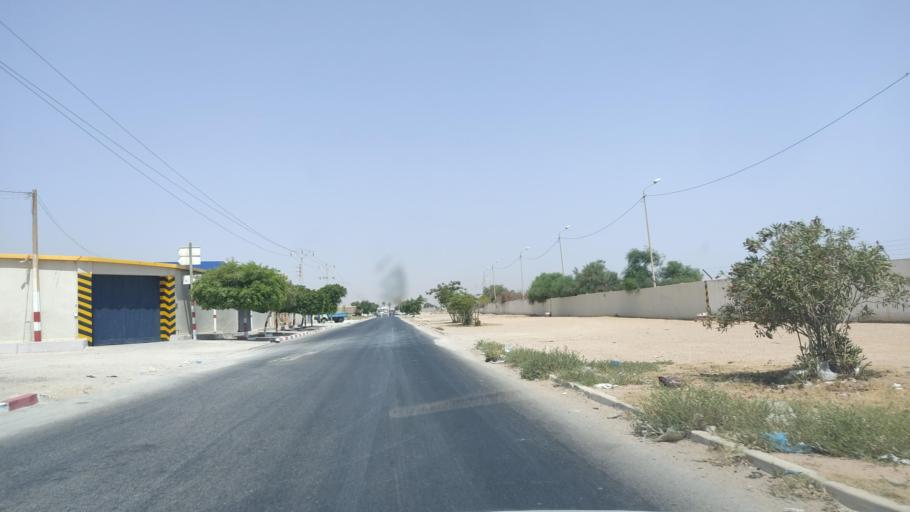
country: TN
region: Safaqis
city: Sfax
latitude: 34.6959
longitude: 10.7226
